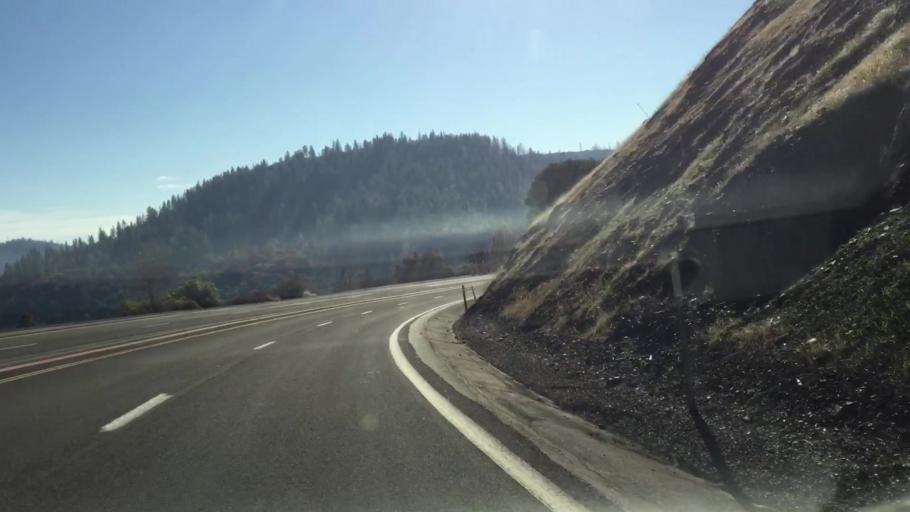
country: US
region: California
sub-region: Butte County
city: Berry Creek
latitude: 39.6706
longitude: -121.5262
